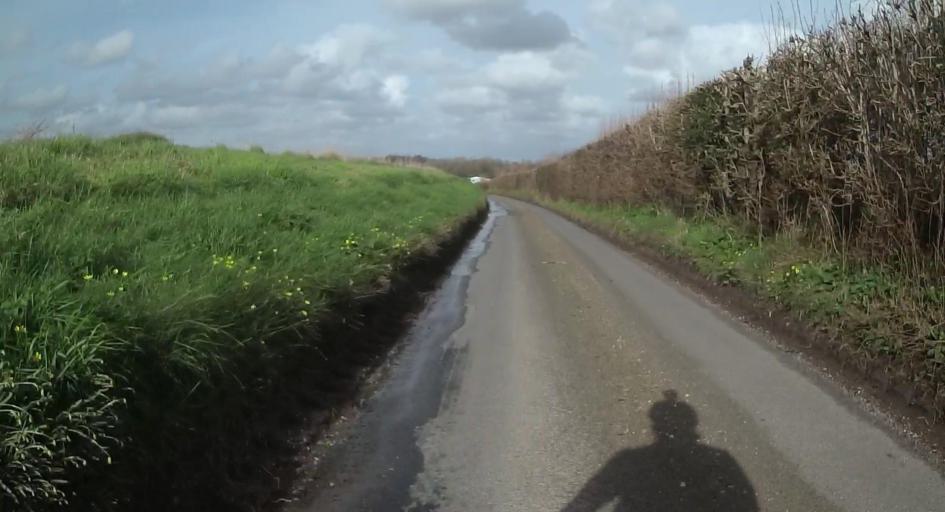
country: GB
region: England
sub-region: Hampshire
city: Kingsclere
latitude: 51.3415
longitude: -1.2420
